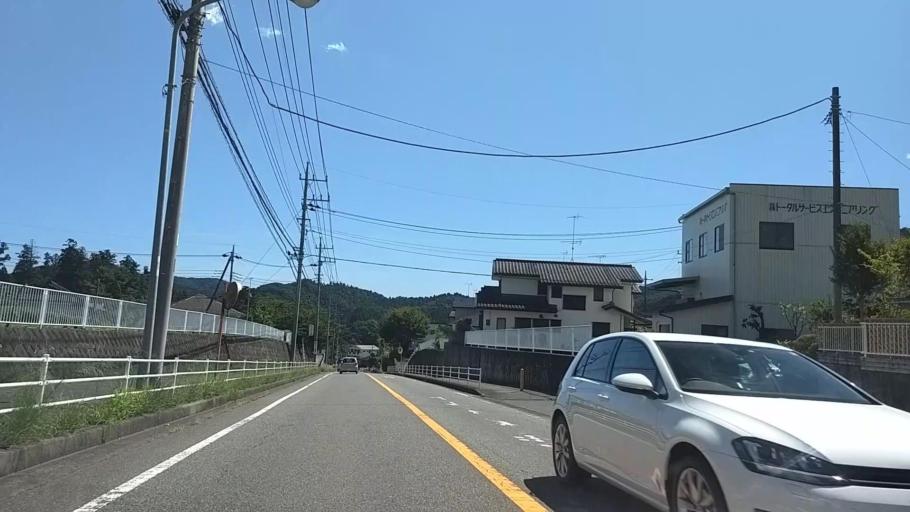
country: JP
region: Tokyo
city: Hachioji
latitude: 35.5681
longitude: 139.2425
